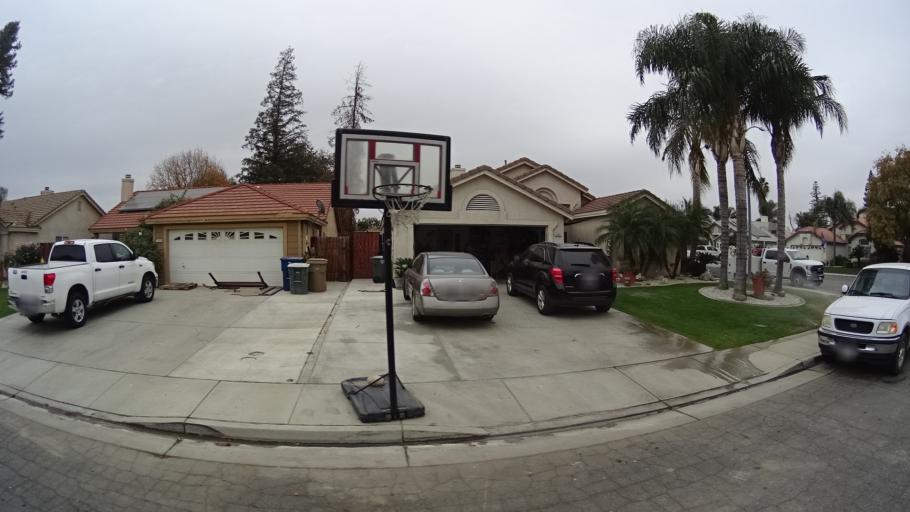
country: US
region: California
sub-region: Kern County
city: Greenfield
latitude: 35.2872
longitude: -119.0444
